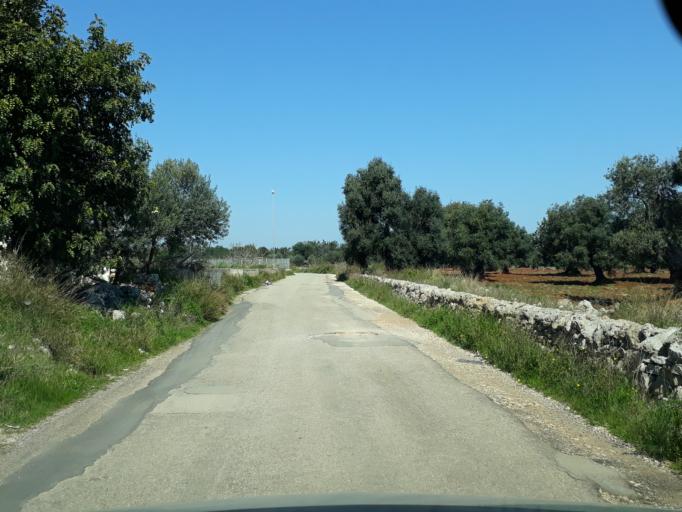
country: IT
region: Apulia
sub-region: Provincia di Brindisi
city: Fasano
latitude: 40.8282
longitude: 17.3817
